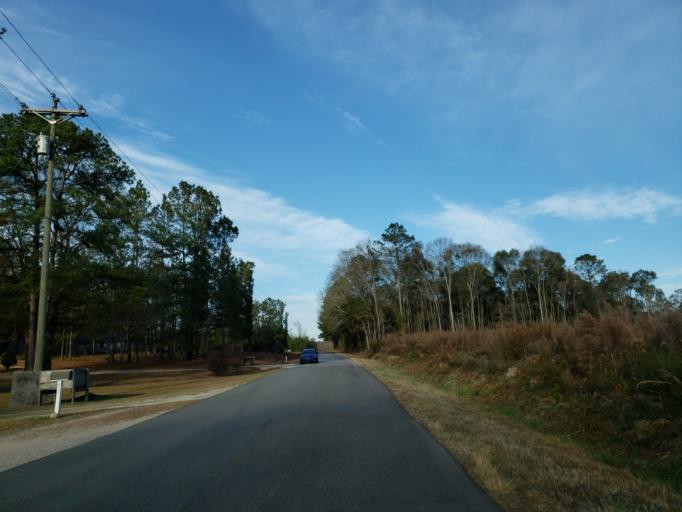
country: US
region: Mississippi
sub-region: Wayne County
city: Belmont
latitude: 31.5061
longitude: -88.5073
